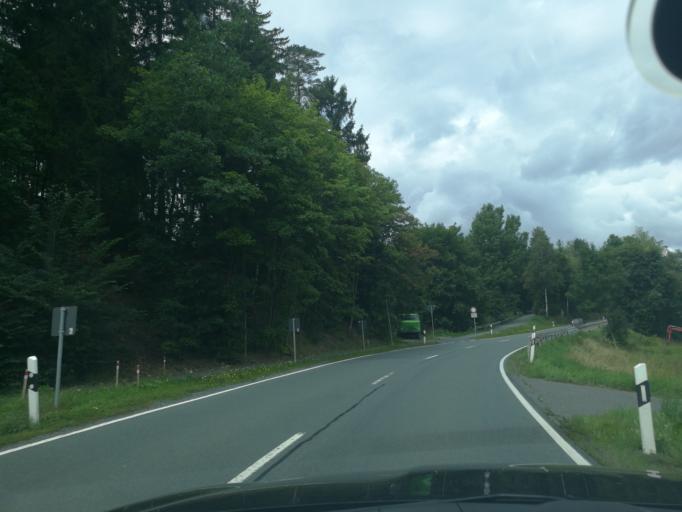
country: DE
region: Saxony
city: Adorf
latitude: 50.3455
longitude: 12.2374
